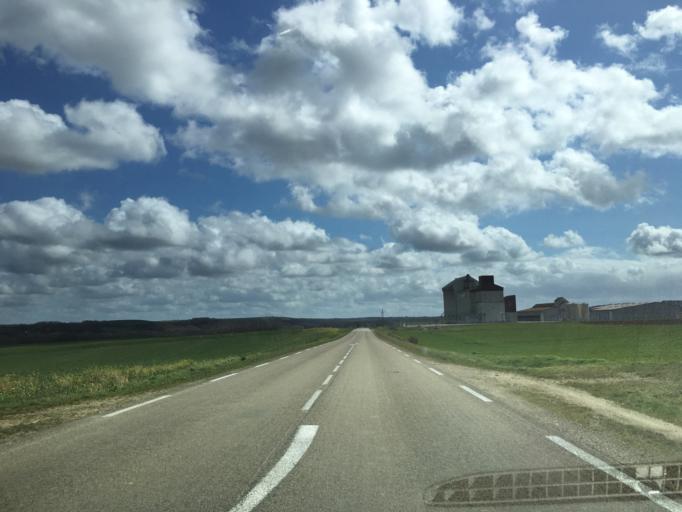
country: FR
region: Bourgogne
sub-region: Departement de l'Yonne
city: Aillant-sur-Tholon
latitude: 47.8523
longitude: 3.3775
